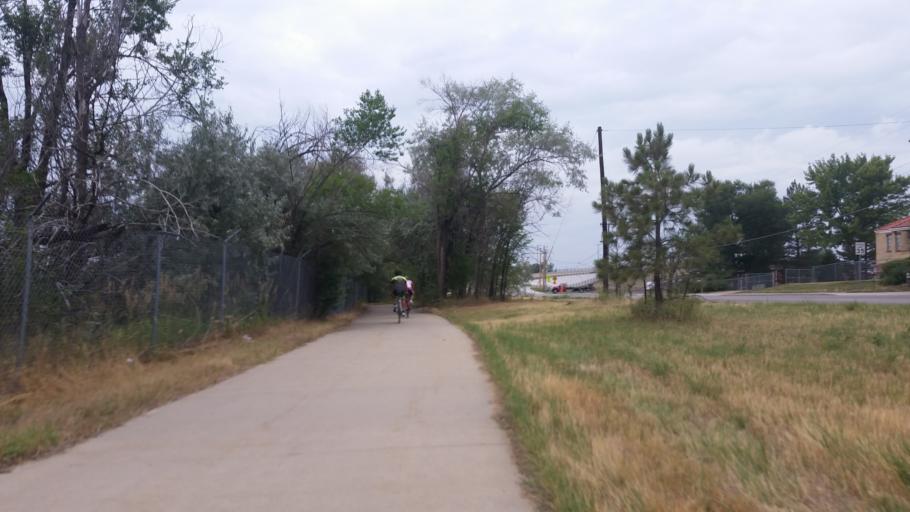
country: US
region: Colorado
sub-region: Adams County
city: Twin Lakes
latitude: 39.8143
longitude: -105.0092
